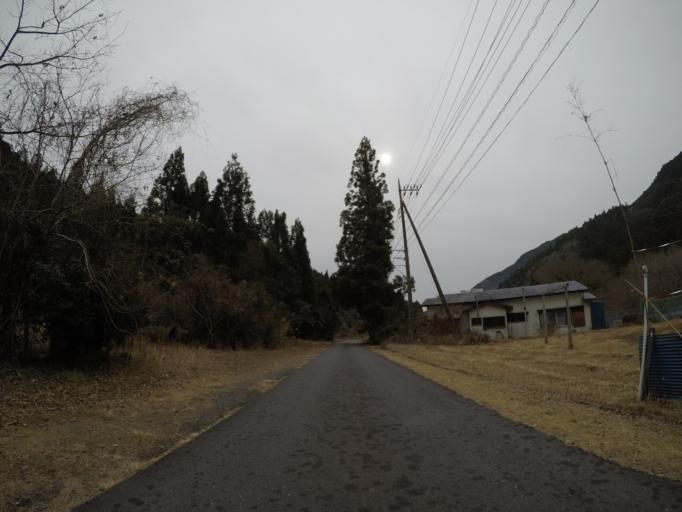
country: JP
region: Shizuoka
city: Fujinomiya
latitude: 35.2717
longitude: 138.5301
